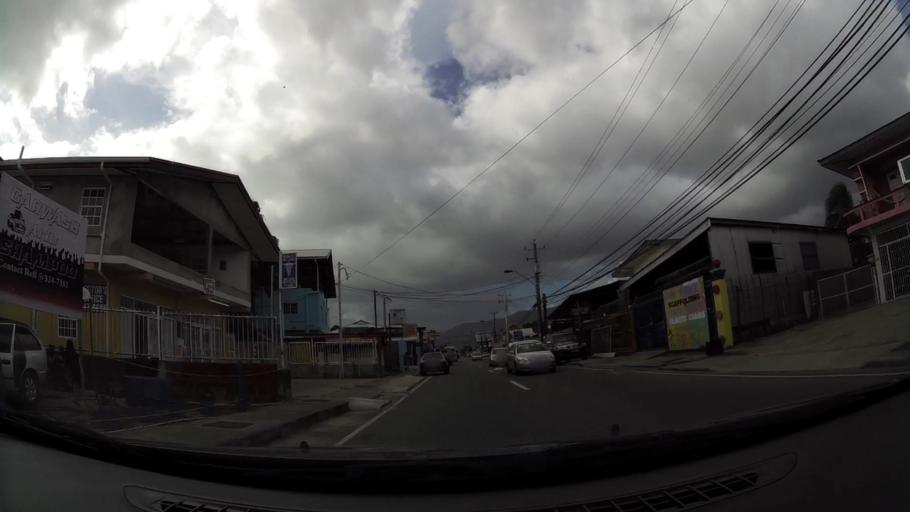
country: TT
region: Tunapuna/Piarco
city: Arouca
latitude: 10.6381
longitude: -61.3476
